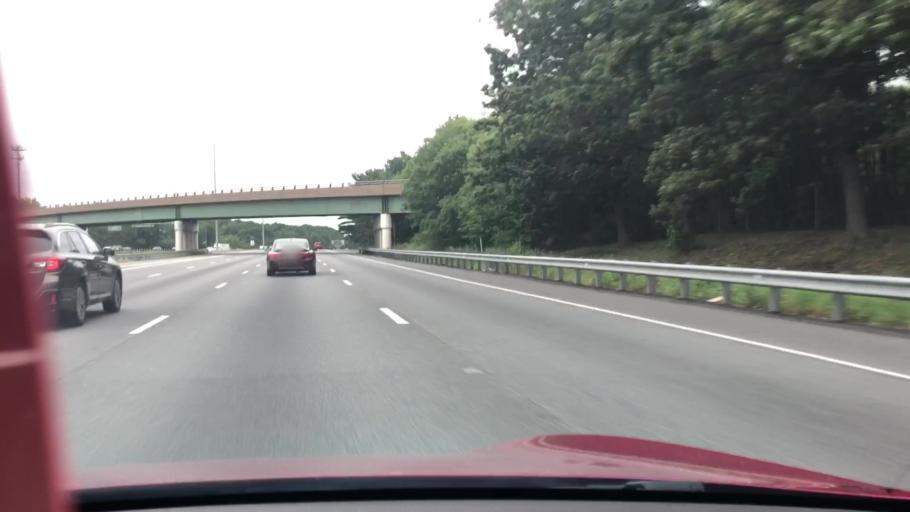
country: US
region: Delaware
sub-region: New Castle County
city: Brookside
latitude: 39.6594
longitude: -75.6970
